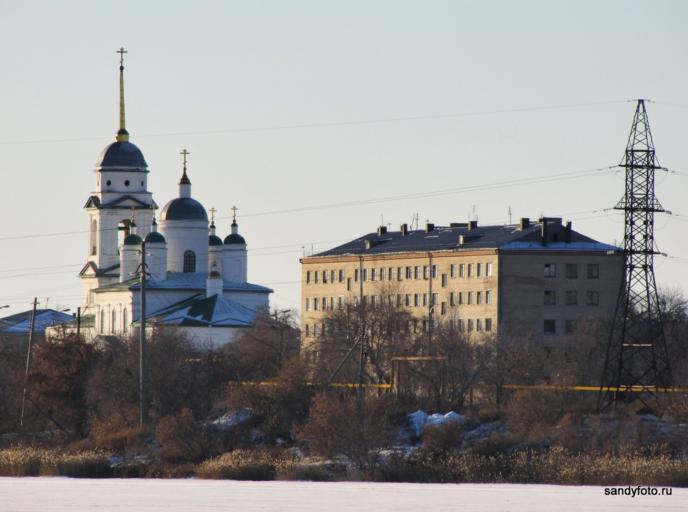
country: RU
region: Chelyabinsk
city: Troitsk
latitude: 54.0792
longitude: 61.5732
